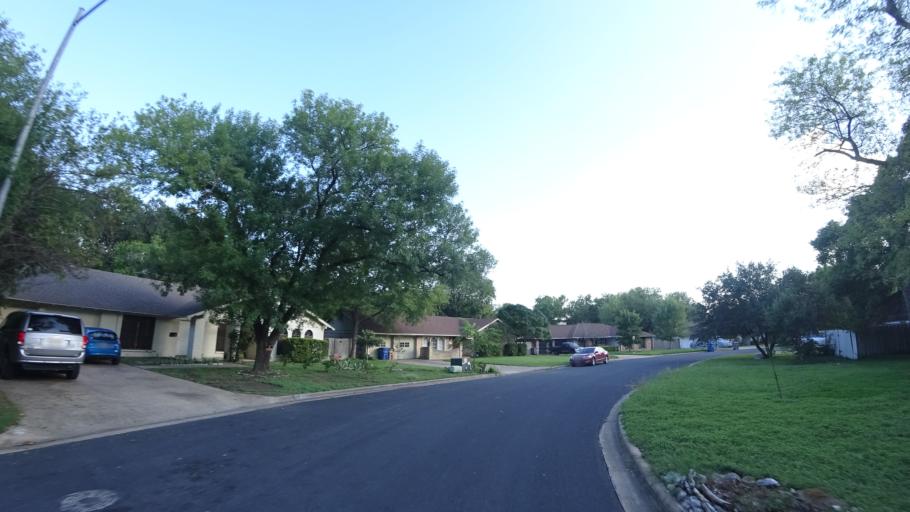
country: US
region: Texas
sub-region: Travis County
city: Wells Branch
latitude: 30.3634
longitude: -97.7002
